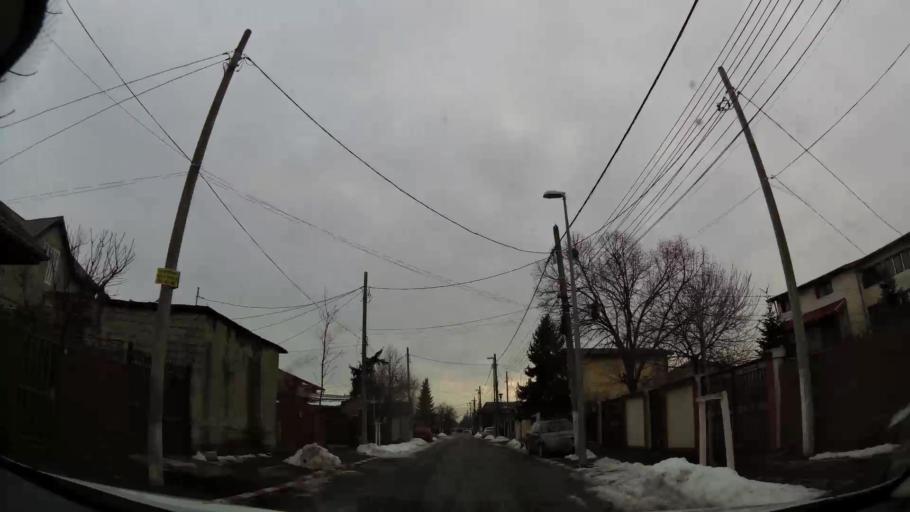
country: RO
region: Ilfov
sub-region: Voluntari City
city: Voluntari
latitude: 44.4902
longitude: 26.1781
